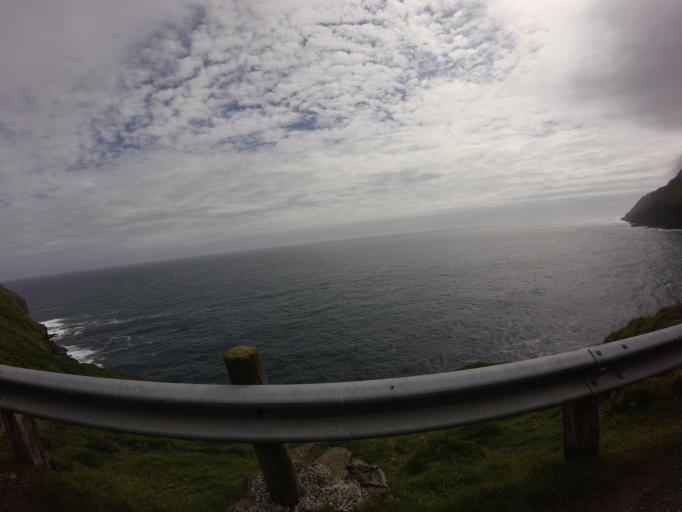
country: FO
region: Sandoy
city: Sandur
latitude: 61.7876
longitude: -6.6660
